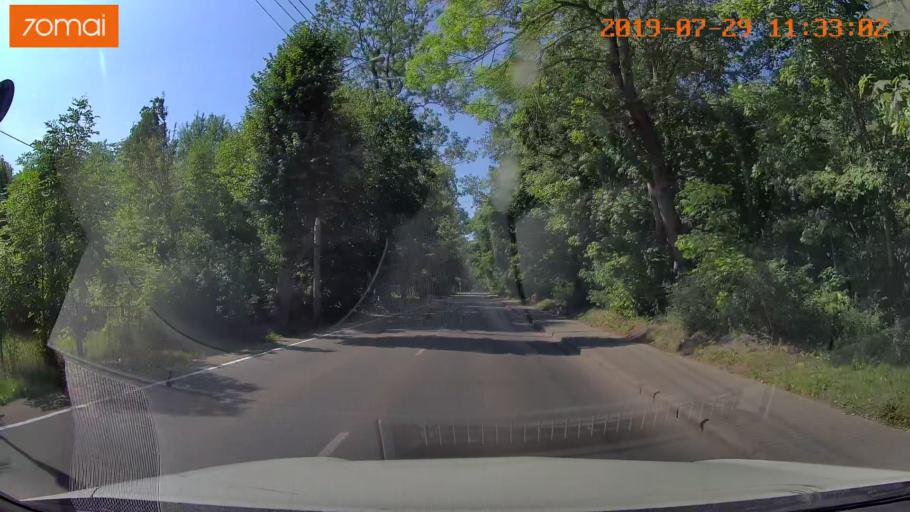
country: RU
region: Kaliningrad
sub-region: Gorod Kaliningrad
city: Kaliningrad
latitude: 54.6676
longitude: 20.5437
